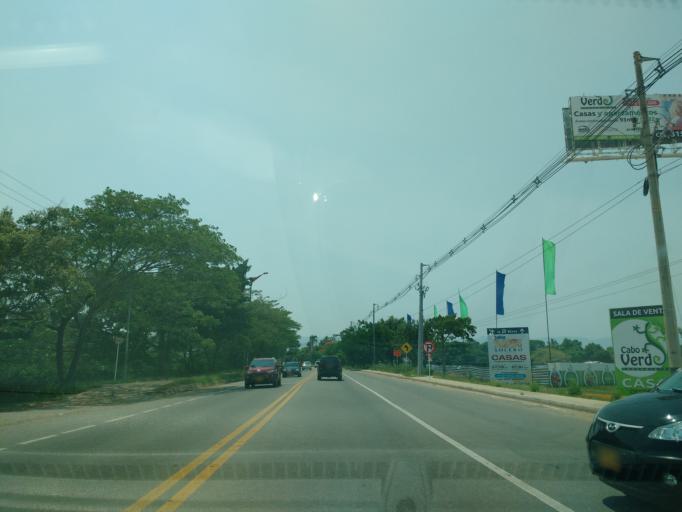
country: CO
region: Cundinamarca
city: Ricaurte
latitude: 4.2920
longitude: -74.7803
